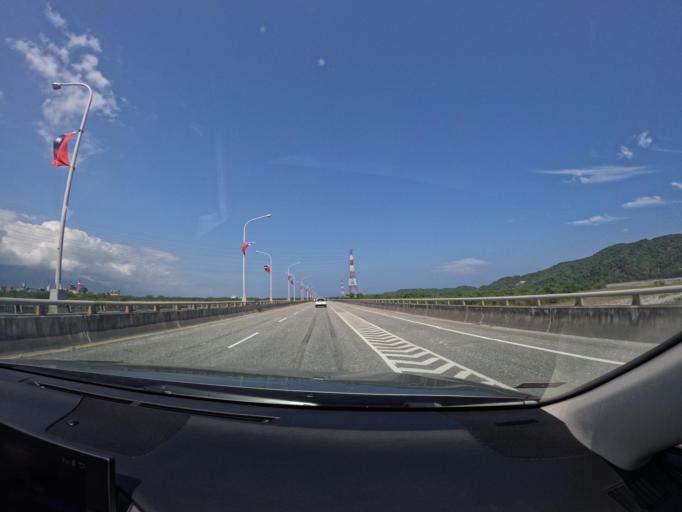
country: TW
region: Taiwan
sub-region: Hualien
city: Hualian
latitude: 23.9193
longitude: 121.5845
